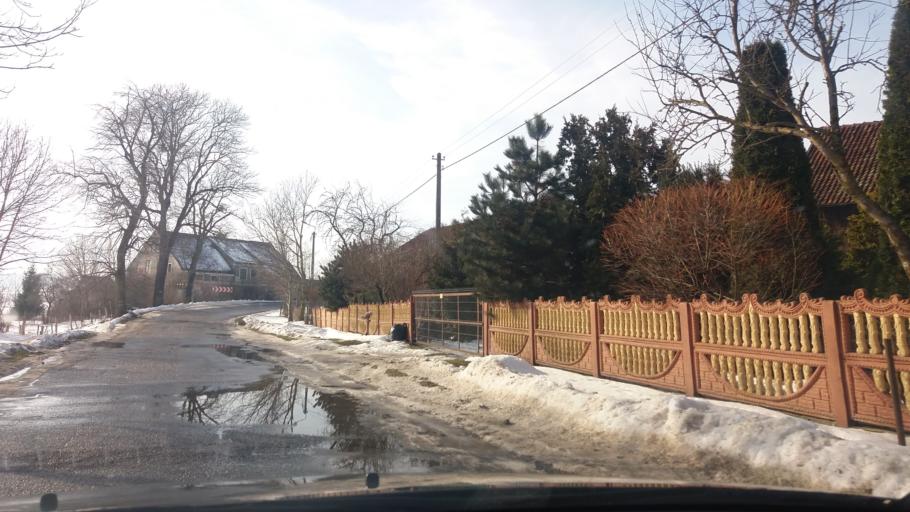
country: PL
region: Warmian-Masurian Voivodeship
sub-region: Powiat bartoszycki
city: Bisztynek
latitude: 54.1012
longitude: 20.8022
